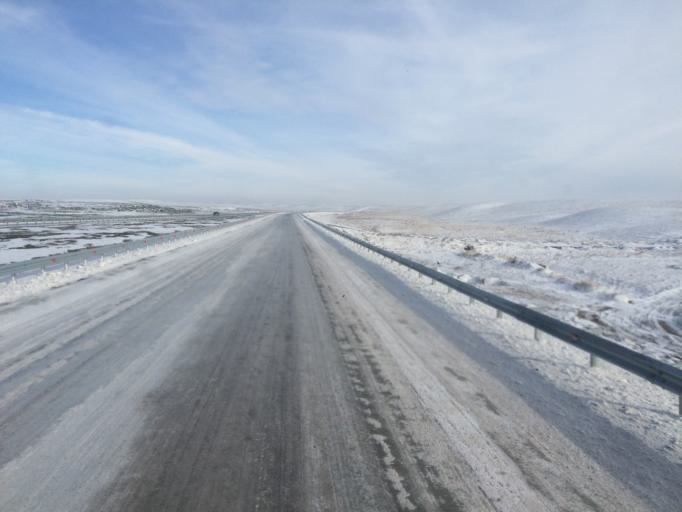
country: KZ
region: Zhambyl
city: Georgiyevka
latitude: 43.3540
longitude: 74.5661
